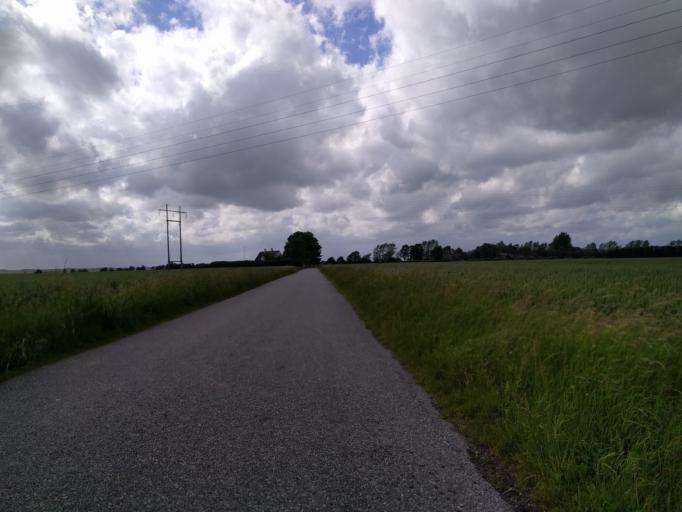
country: DK
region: South Denmark
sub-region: Odense Kommune
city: Bullerup
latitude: 55.4503
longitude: 10.5092
